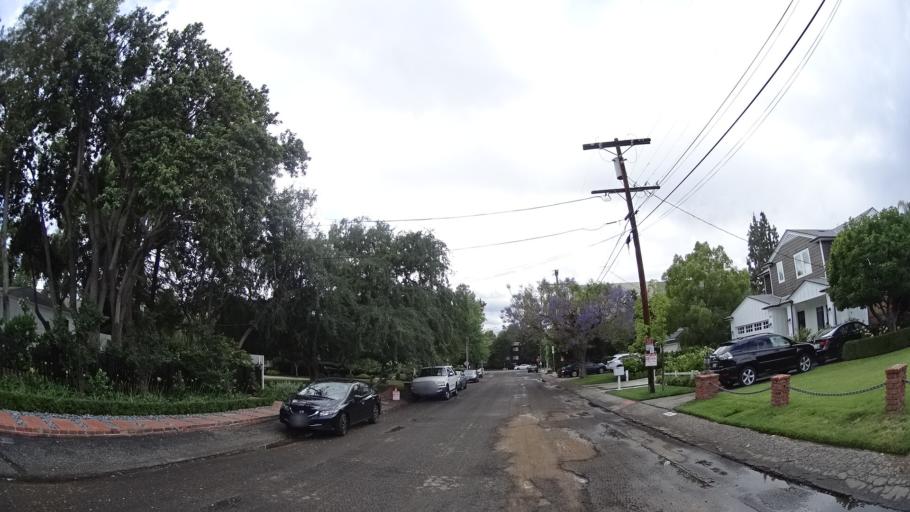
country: US
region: California
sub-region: Los Angeles County
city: Sherman Oaks
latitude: 34.1549
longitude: -118.4125
